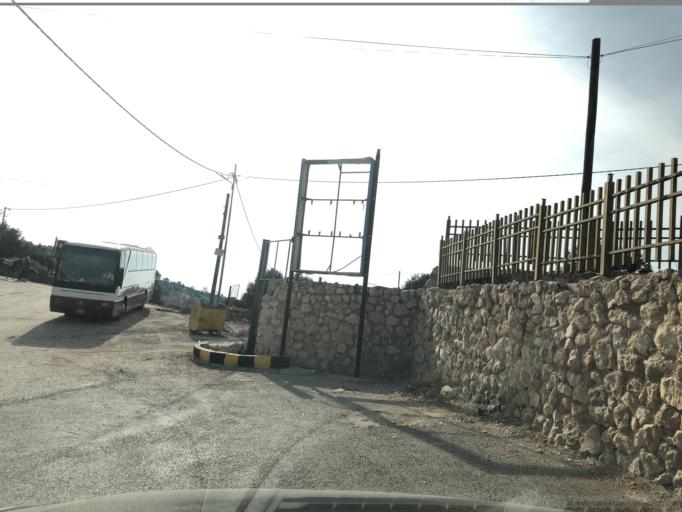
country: JO
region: Ajlun
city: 'Ajlun
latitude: 32.3281
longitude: 35.7271
